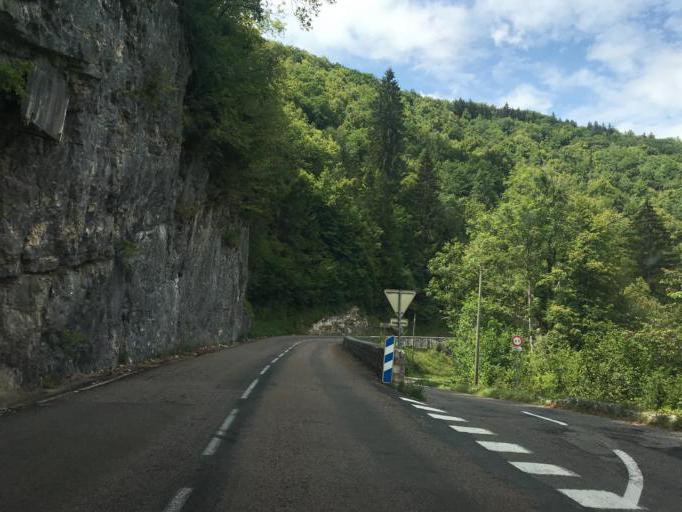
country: FR
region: Franche-Comte
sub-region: Departement du Jura
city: Saint-Claude
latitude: 46.4082
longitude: 5.8642
